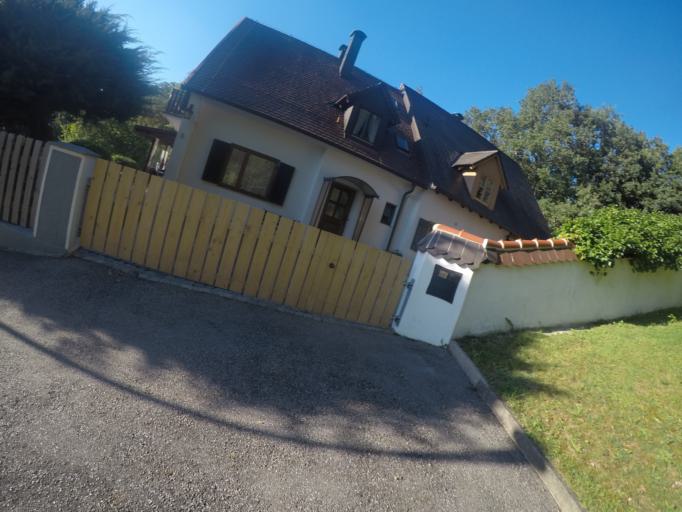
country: DE
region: Bavaria
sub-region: Lower Bavaria
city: Landshut
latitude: 48.5137
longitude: 12.1570
